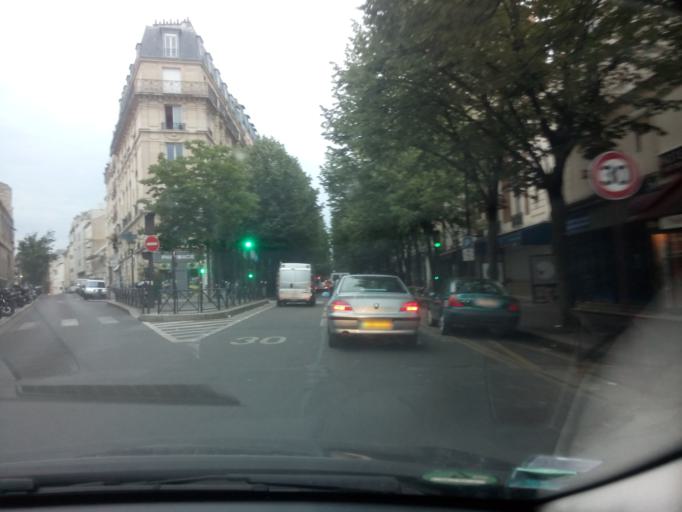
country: FR
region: Ile-de-France
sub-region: Departement du Val-de-Marne
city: Le Kremlin-Bicetre
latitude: 48.8282
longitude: 2.3527
